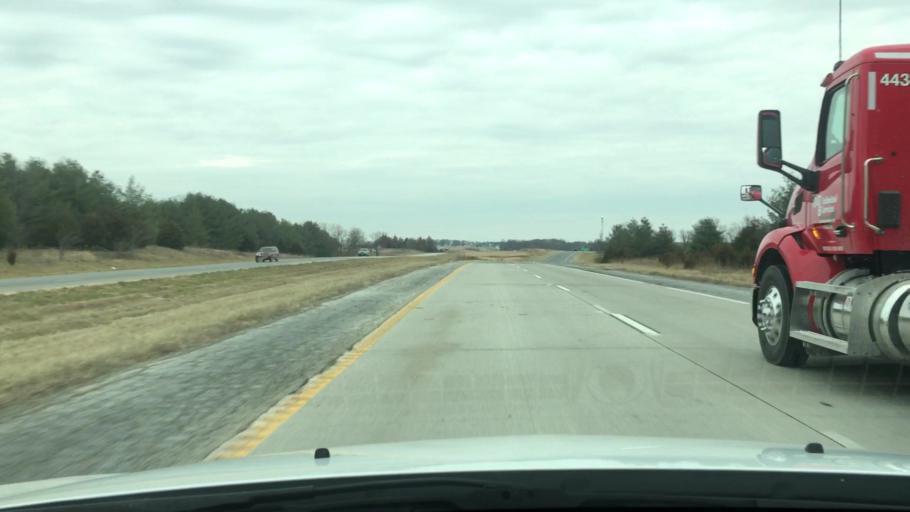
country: US
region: Missouri
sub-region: Audrain County
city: Mexico
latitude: 39.0947
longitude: -91.8988
